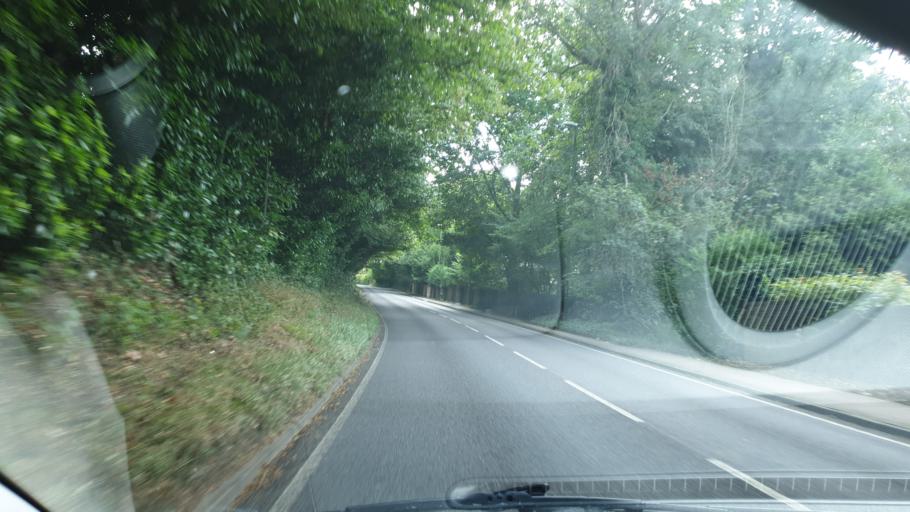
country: GB
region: England
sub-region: West Sussex
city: East Grinstead
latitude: 51.1180
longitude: 0.0118
